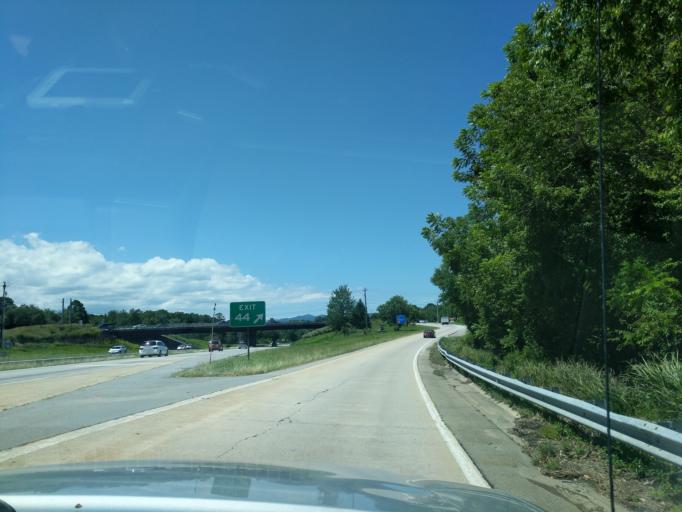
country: US
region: North Carolina
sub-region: Henderson County
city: Fletcher
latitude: 35.3989
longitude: -82.5062
